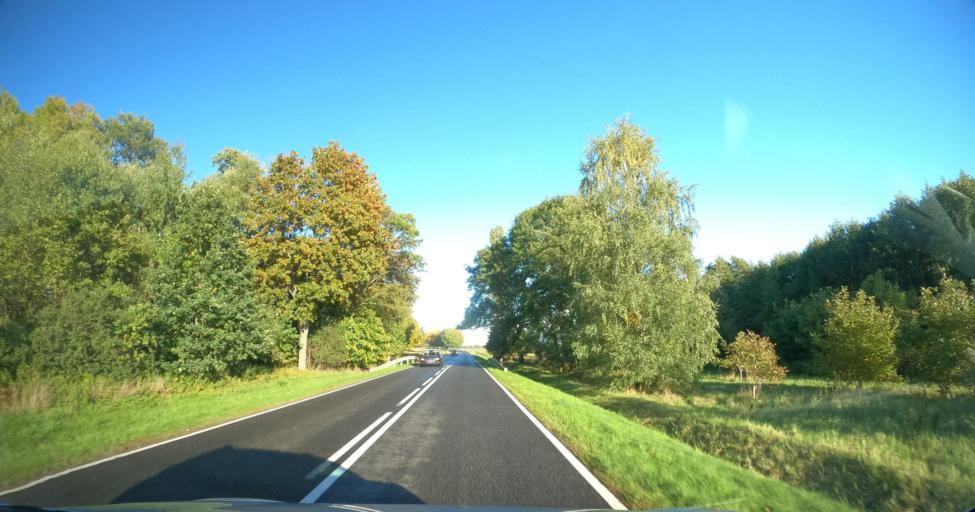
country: PL
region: Lubusz
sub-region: Powiat zielonogorski
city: Zabor
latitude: 51.9278
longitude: 15.6411
